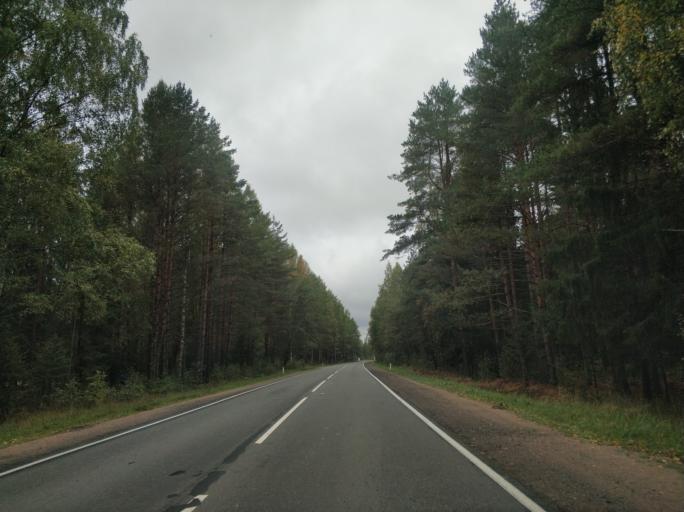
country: RU
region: Leningrad
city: Borisova Griva
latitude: 60.0903
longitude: 30.8607
